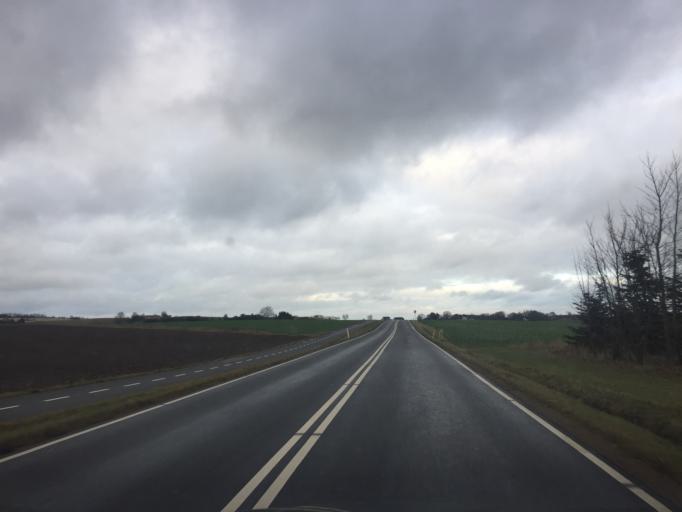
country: DK
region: Zealand
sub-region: Holbaek Kommune
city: Tollose
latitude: 55.6003
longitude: 11.6989
